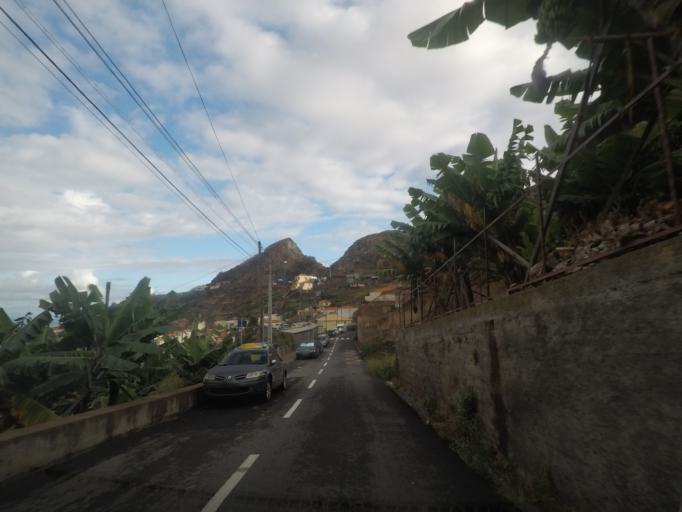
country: PT
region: Madeira
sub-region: Ribeira Brava
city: Campanario
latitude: 32.6583
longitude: -16.9974
